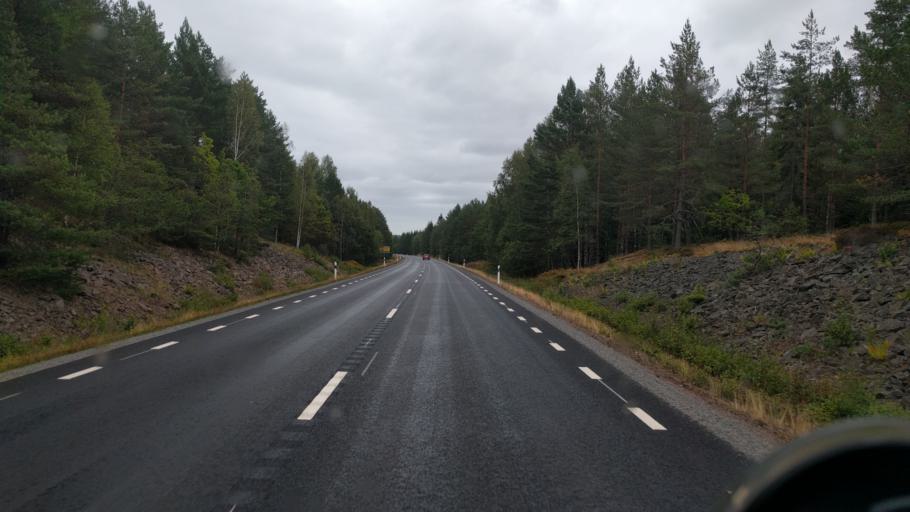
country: SE
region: Kalmar
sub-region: Vasterviks Kommun
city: Ankarsrum
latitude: 57.7226
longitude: 16.3719
